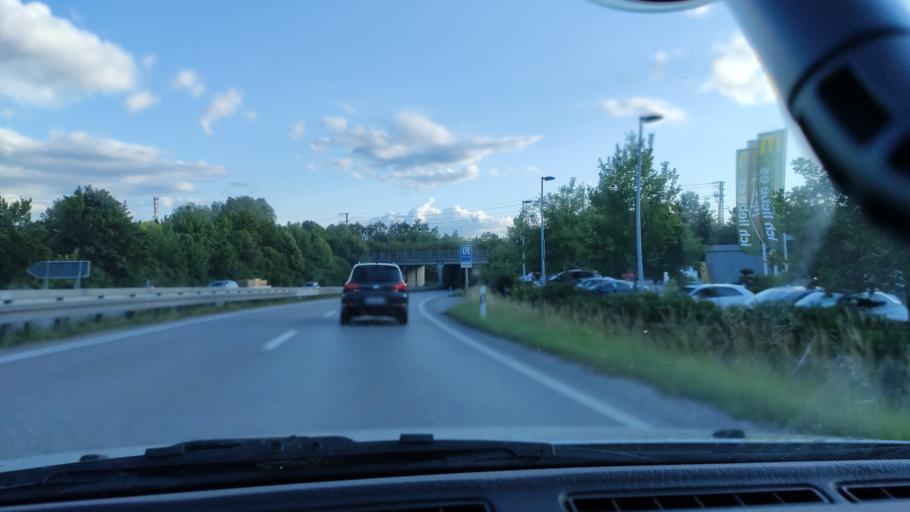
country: DE
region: Bavaria
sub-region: Swabia
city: Gersthofen
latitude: 48.3984
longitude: 10.8693
